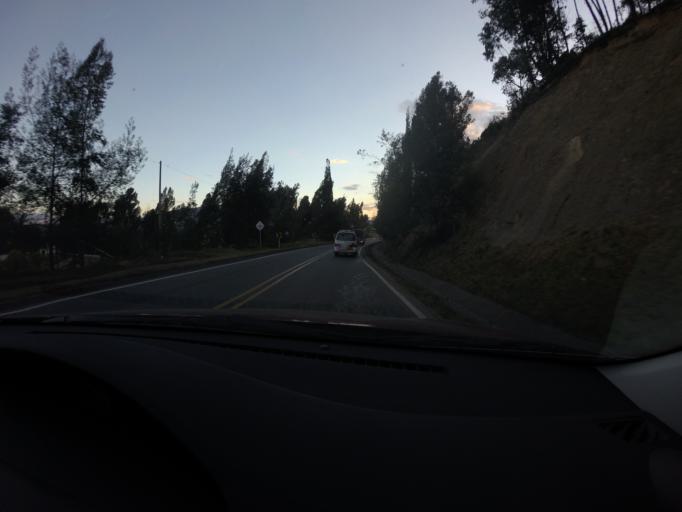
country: CO
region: Cundinamarca
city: Nemocon
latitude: 5.1121
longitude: -73.9091
